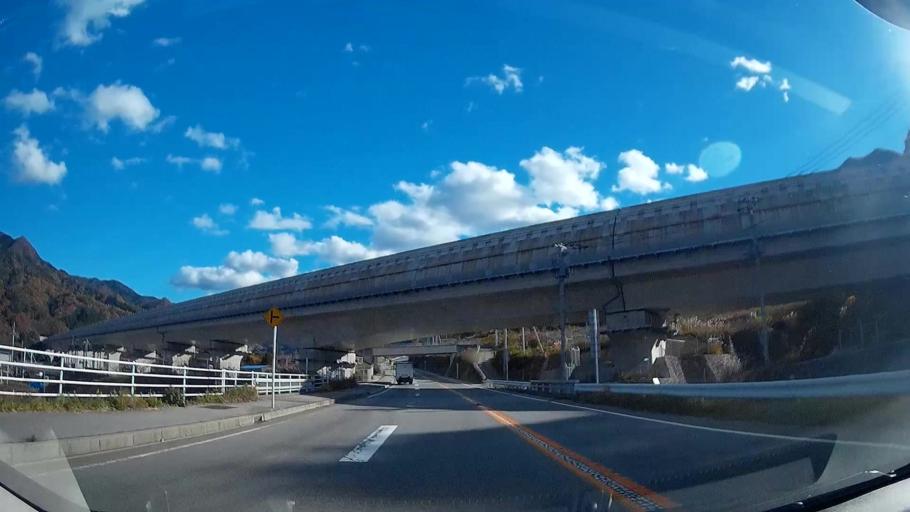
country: JP
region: Yamanashi
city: Isawa
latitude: 35.6044
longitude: 138.7044
